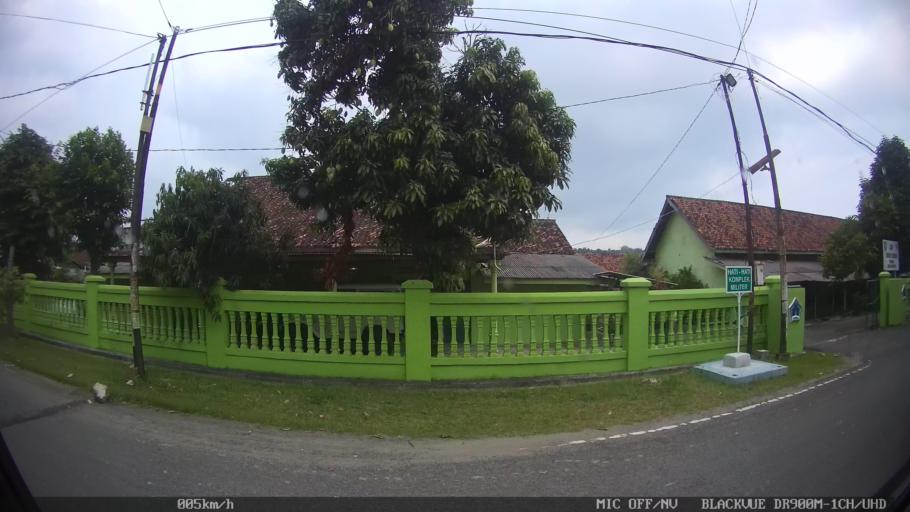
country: ID
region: Lampung
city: Bandarlampung
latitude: -5.4286
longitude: 105.2738
